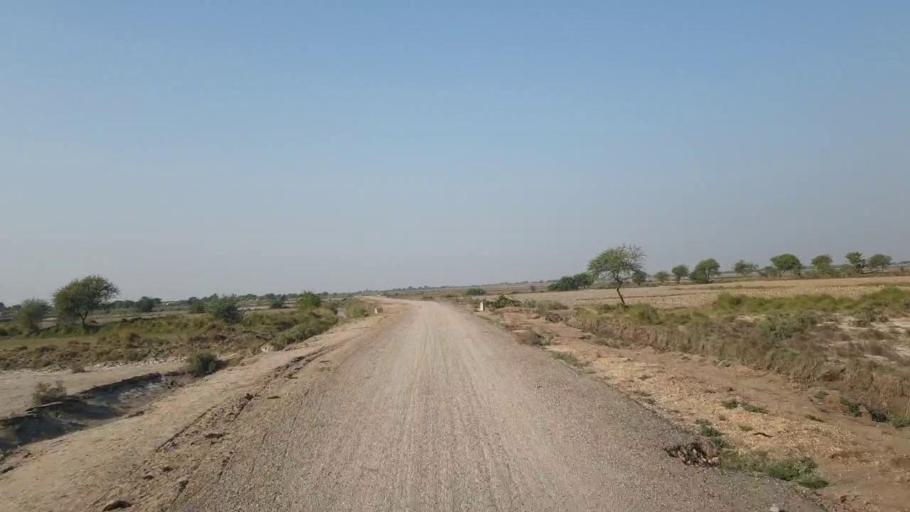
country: PK
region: Sindh
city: Kario
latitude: 24.9032
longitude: 68.6206
